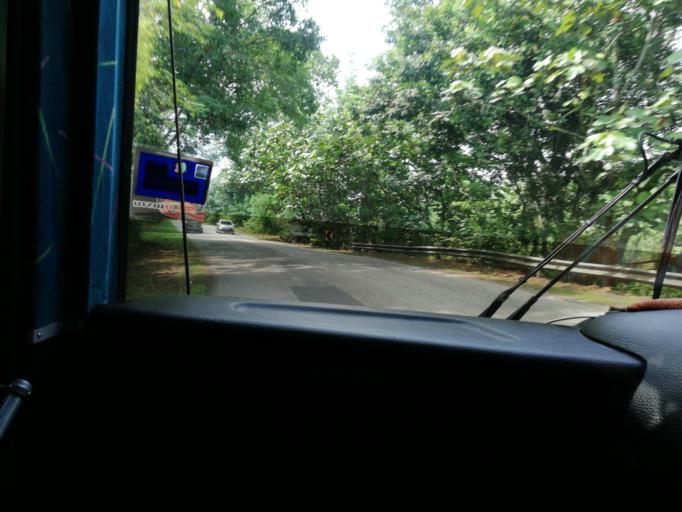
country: MY
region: Kedah
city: Kulim
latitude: 5.3375
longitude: 100.5902
